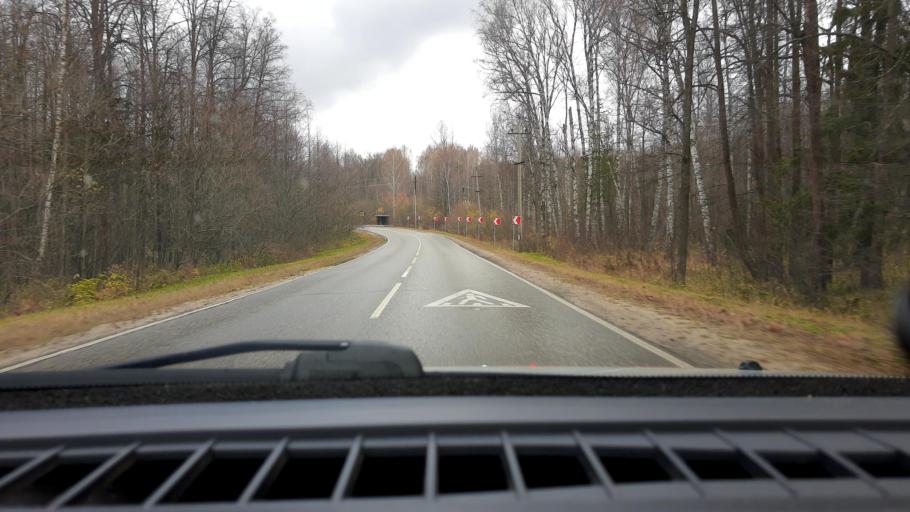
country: RU
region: Nizjnij Novgorod
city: Afonino
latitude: 56.1853
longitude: 44.0230
